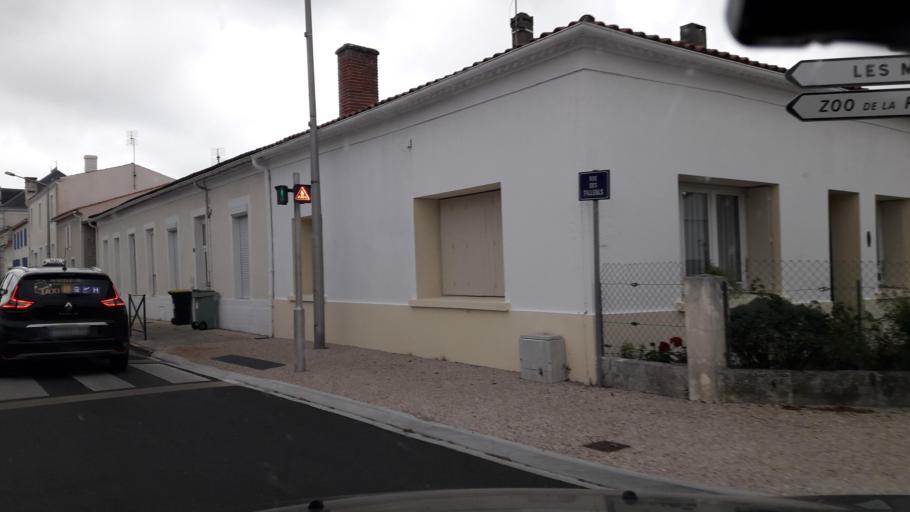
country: FR
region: Poitou-Charentes
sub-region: Departement de la Charente-Maritime
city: Arvert
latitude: 45.7425
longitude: -1.1240
